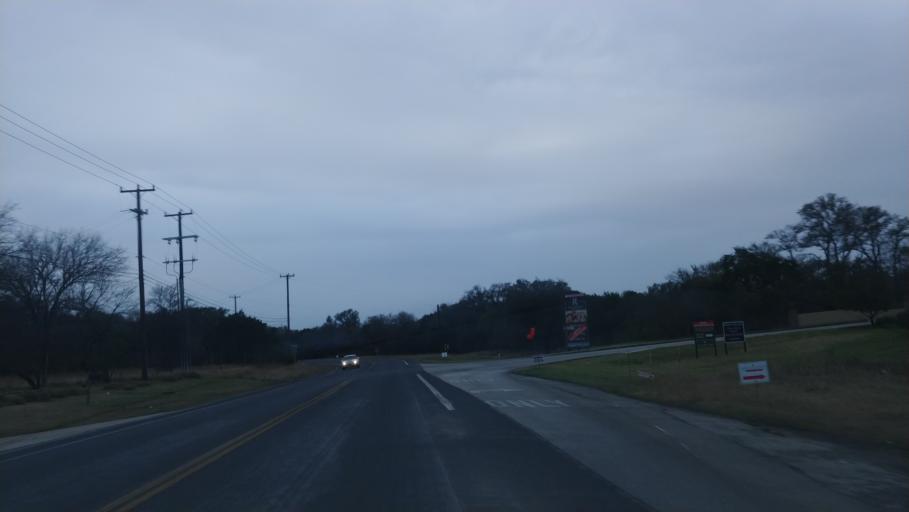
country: US
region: Texas
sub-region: Bexar County
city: Cross Mountain
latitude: 29.6760
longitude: -98.6582
